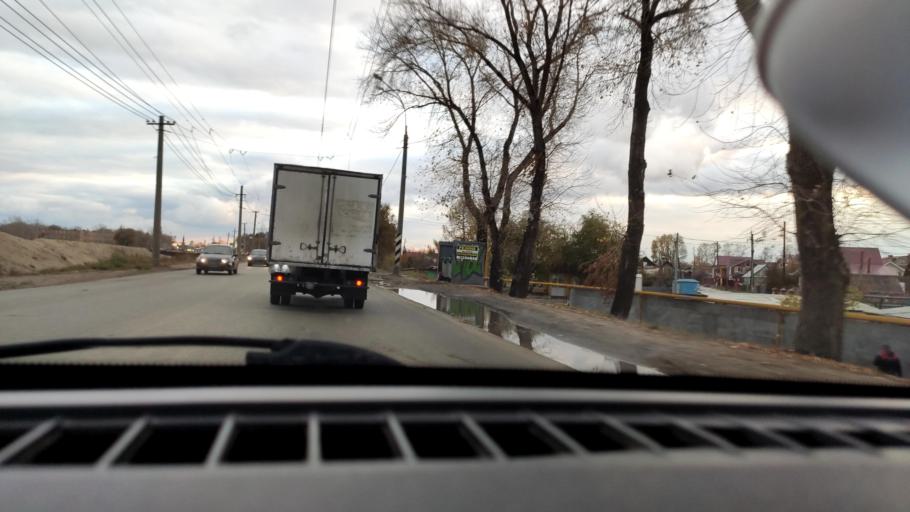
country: RU
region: Samara
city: Samara
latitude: 53.1441
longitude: 50.0973
